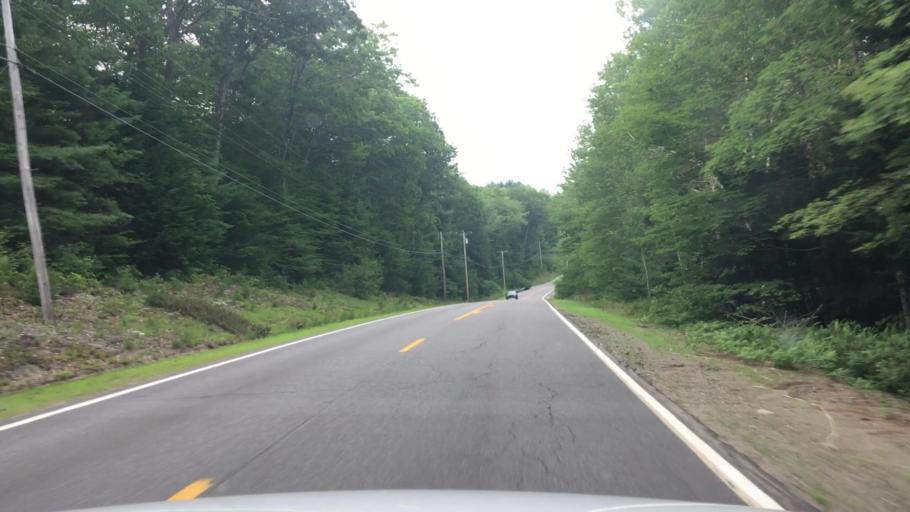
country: US
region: Maine
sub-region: Knox County
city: Washington
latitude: 44.3305
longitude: -69.3534
